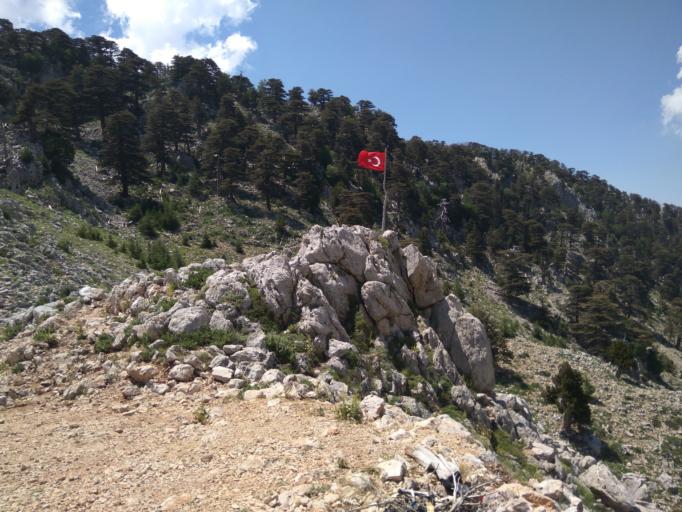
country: TR
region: Antalya
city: Altinyaka
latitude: 36.5431
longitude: 30.4077
